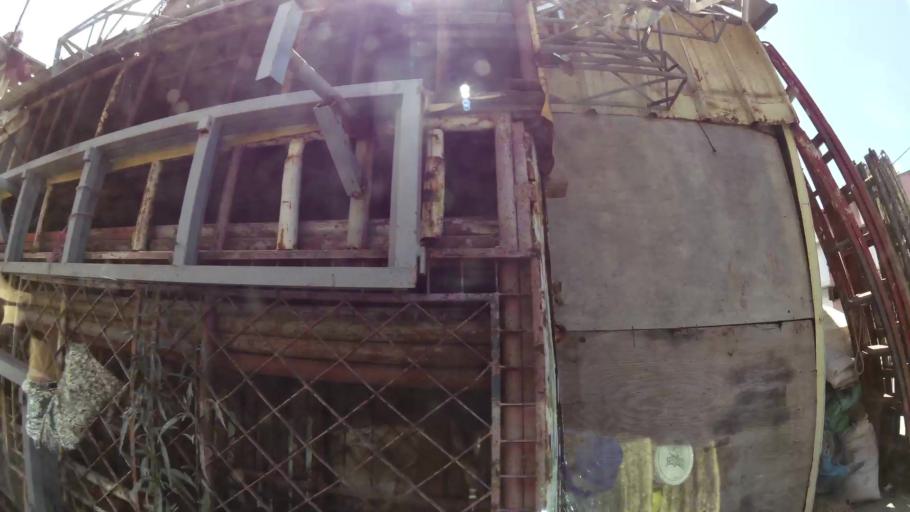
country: MA
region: Gharb-Chrarda-Beni Hssen
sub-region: Kenitra Province
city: Kenitra
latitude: 34.2538
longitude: -6.5553
